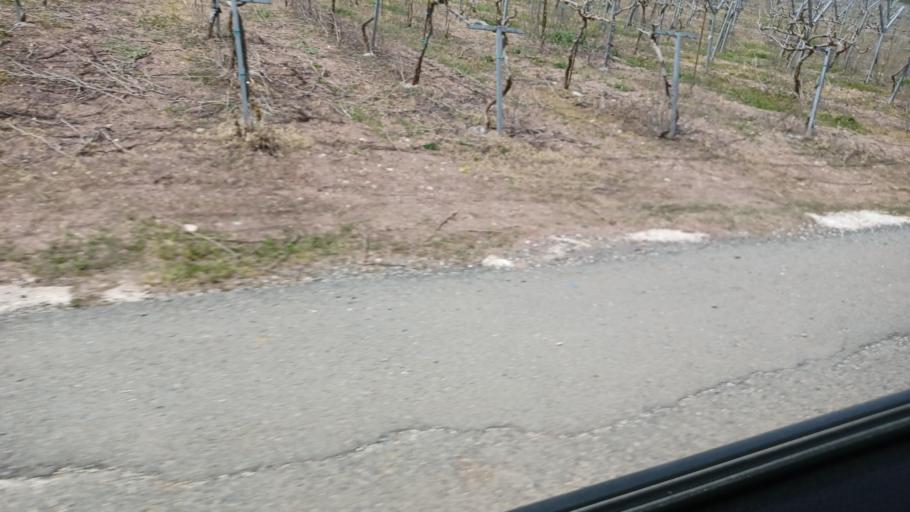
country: CY
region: Pafos
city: Pegeia
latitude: 34.9562
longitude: 32.4022
